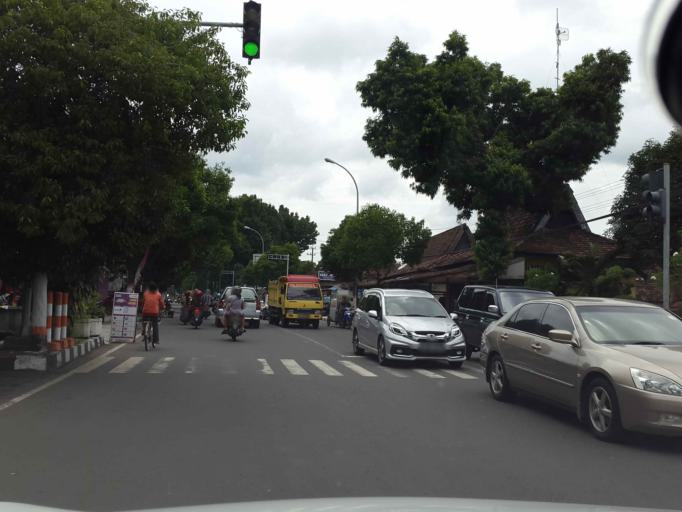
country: ID
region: East Java
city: Mojokerto
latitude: -7.4666
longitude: 112.4480
